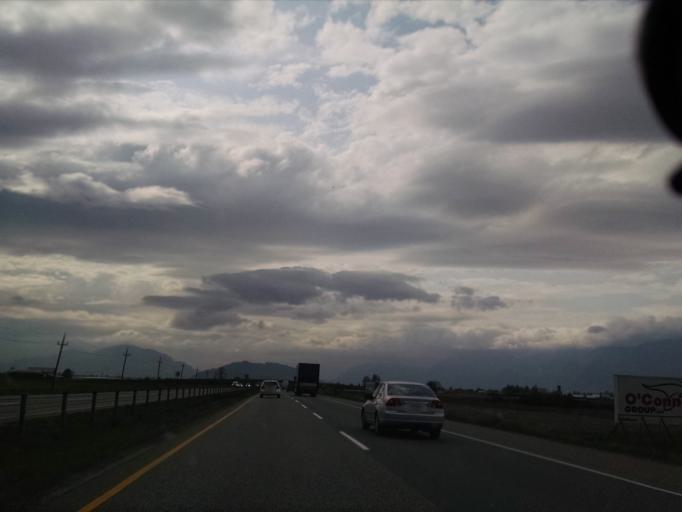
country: CA
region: British Columbia
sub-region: Fraser Valley Regional District
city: Chilliwack
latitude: 49.1550
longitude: -121.8626
